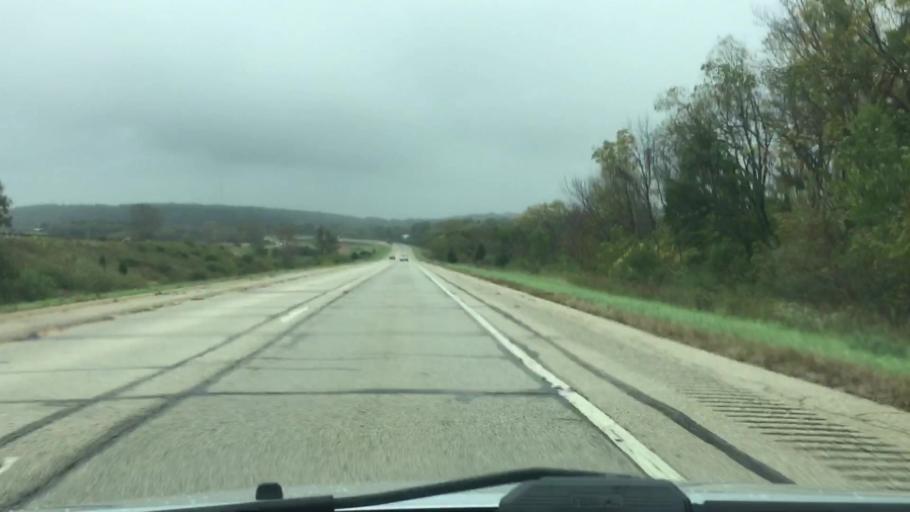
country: US
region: Wisconsin
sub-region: Walworth County
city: Como
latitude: 42.6232
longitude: -88.4649
